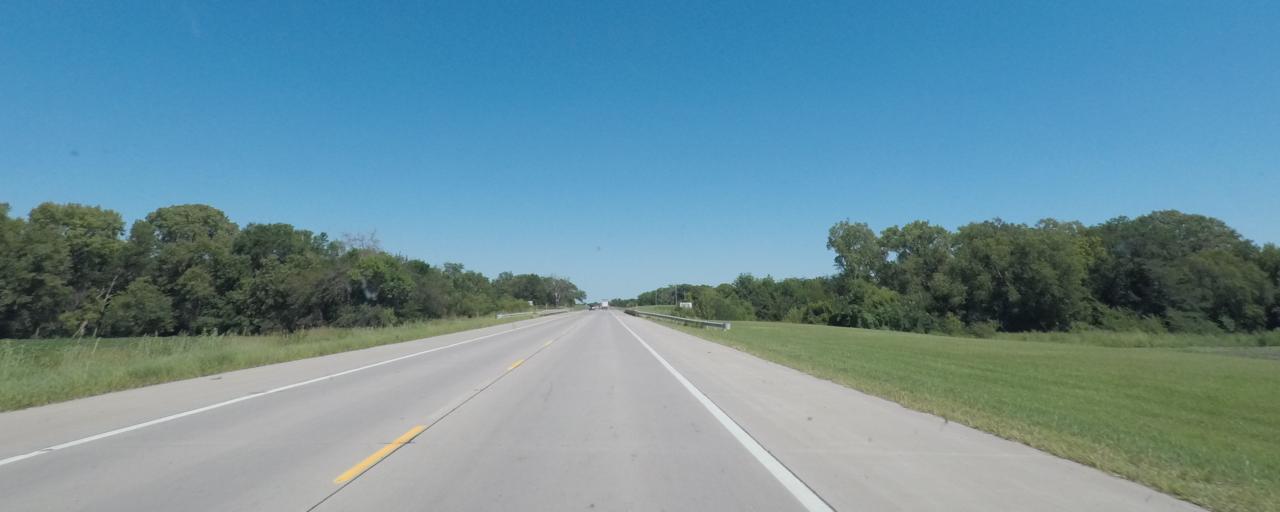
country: US
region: Kansas
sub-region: Lyon County
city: Emporia
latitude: 38.4073
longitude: -96.3028
